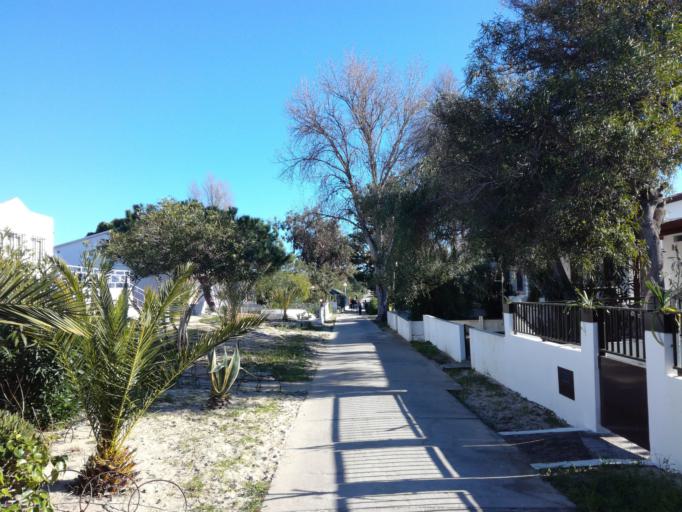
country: PT
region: Faro
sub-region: Olhao
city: Olhao
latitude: 37.0197
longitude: -7.8036
